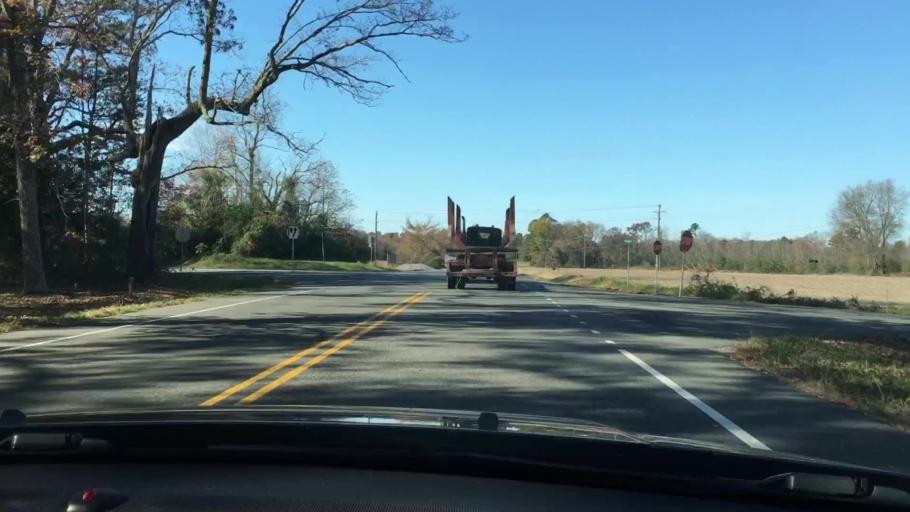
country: US
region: Virginia
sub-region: King William County
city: Central Garage
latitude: 37.7613
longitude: -77.1469
